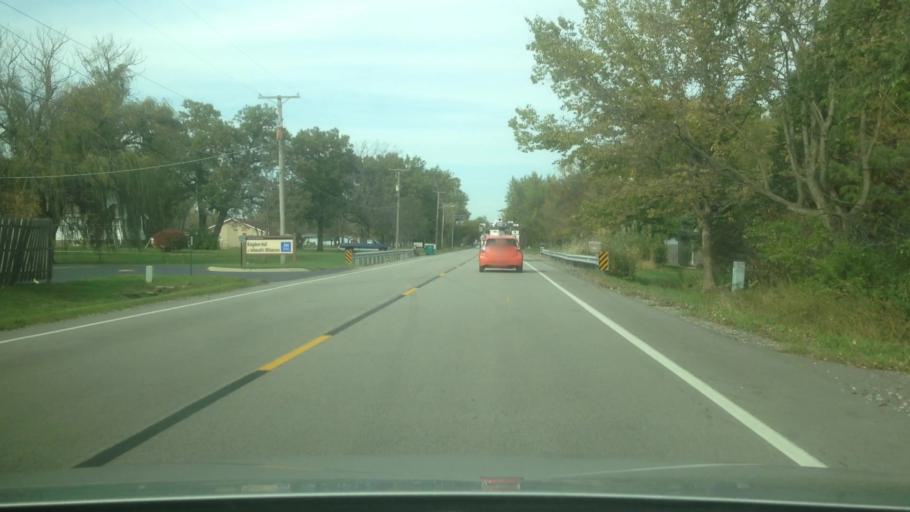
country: US
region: Illinois
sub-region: Will County
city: Wilmington
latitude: 41.3002
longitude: -88.1588
